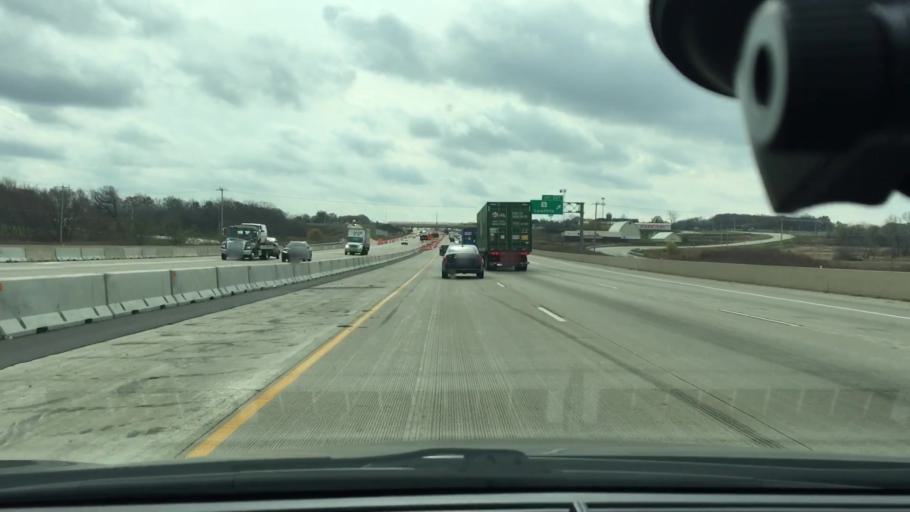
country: US
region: Wisconsin
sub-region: Racine County
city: Caledonia
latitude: 42.8147
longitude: -87.9531
